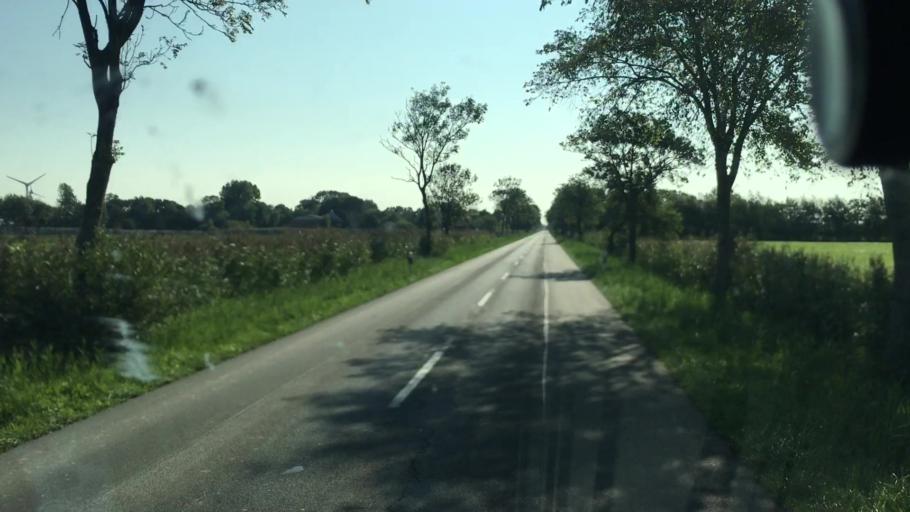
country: DE
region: Lower Saxony
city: Werdum
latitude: 53.6644
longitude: 7.6923
